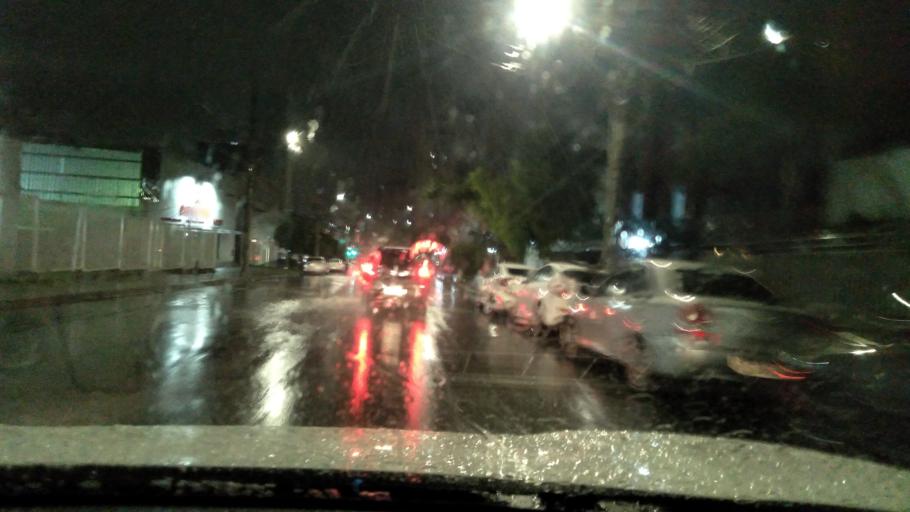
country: BR
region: Minas Gerais
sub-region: Belo Horizonte
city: Belo Horizonte
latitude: -19.8764
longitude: -43.9333
